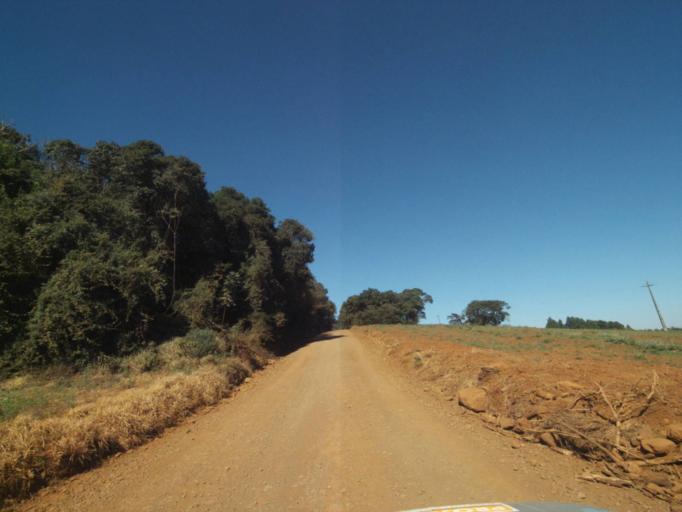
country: BR
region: Parana
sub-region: Tibagi
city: Tibagi
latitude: -24.5896
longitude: -50.6064
